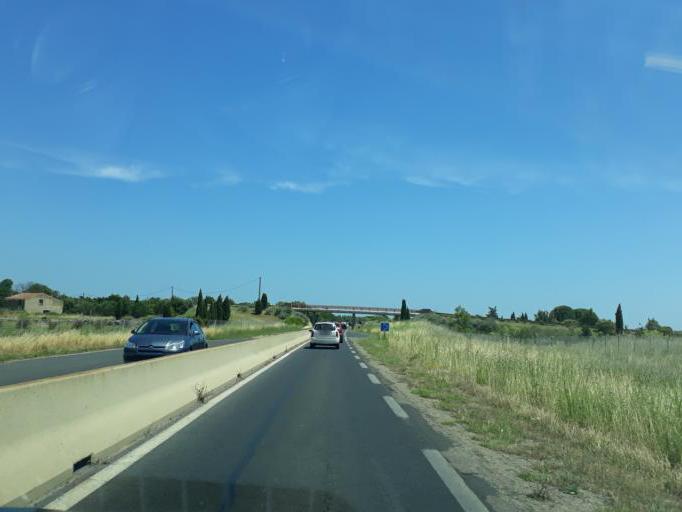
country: FR
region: Languedoc-Roussillon
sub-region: Departement de l'Herault
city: Vias
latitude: 43.3094
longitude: 3.4055
